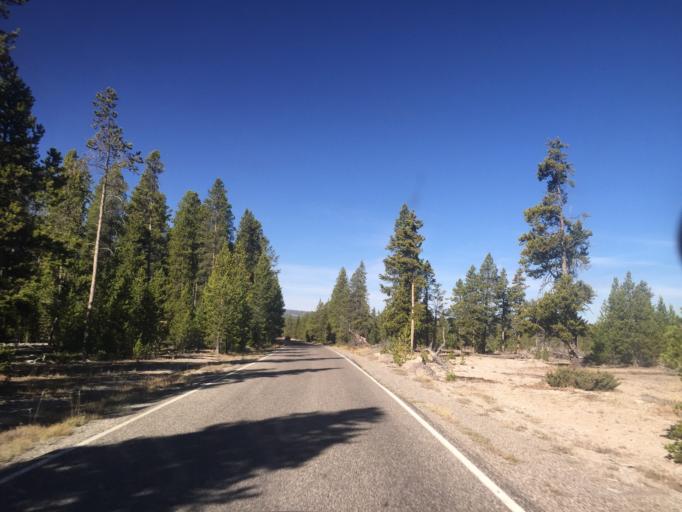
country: US
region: Montana
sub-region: Gallatin County
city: West Yellowstone
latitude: 44.5470
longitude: -110.7961
